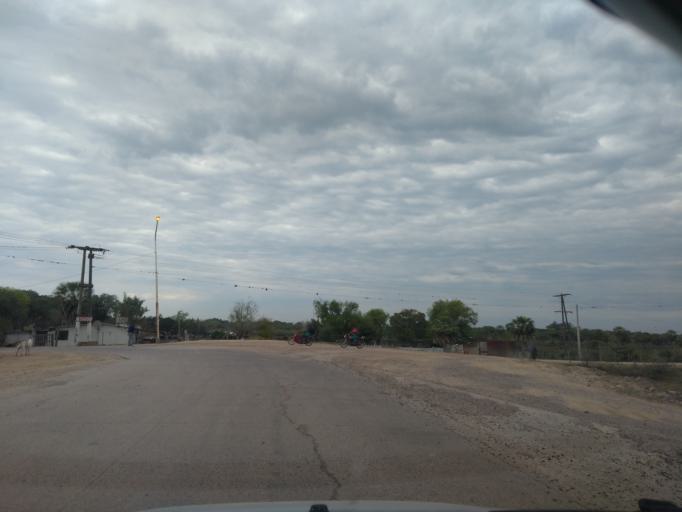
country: AR
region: Chaco
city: Puerto Vilelas
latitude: -27.5356
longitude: -58.9241
